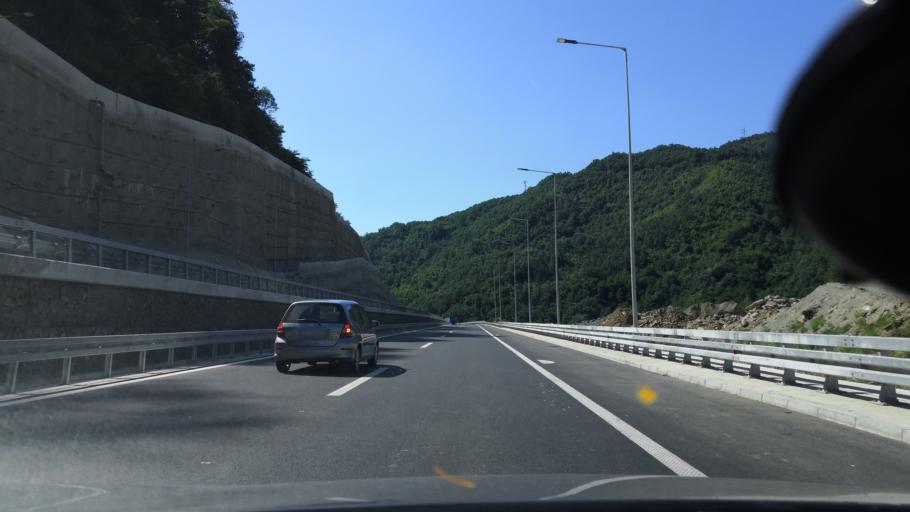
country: RS
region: Central Serbia
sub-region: Jablanicki Okrug
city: Vlasotince
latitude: 42.8695
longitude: 22.1037
